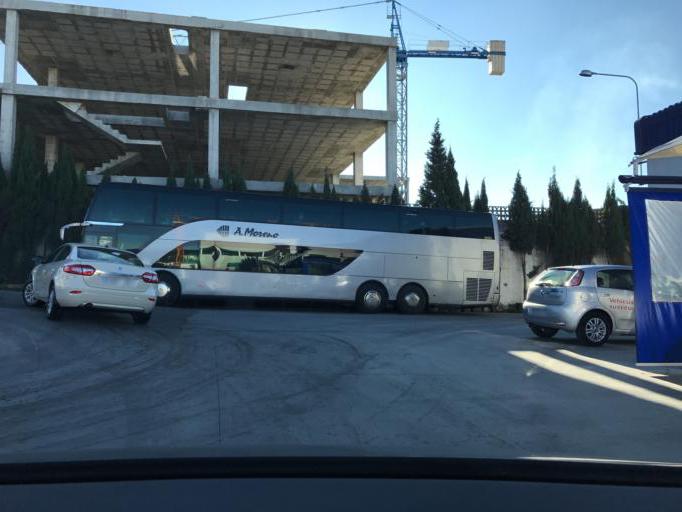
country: ES
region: Andalusia
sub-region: Provincia de Granada
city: Albolote
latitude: 37.2303
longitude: -3.6467
